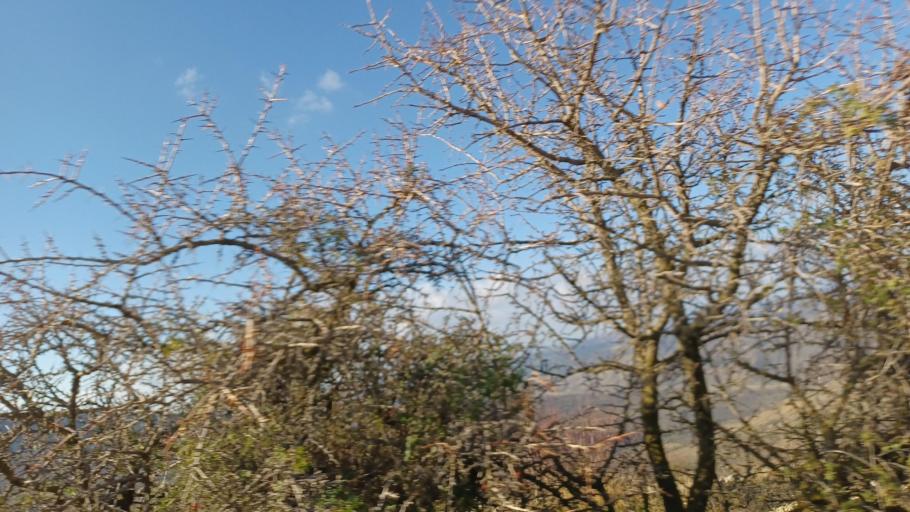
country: CY
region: Limassol
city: Pachna
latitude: 34.8365
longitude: 32.6833
